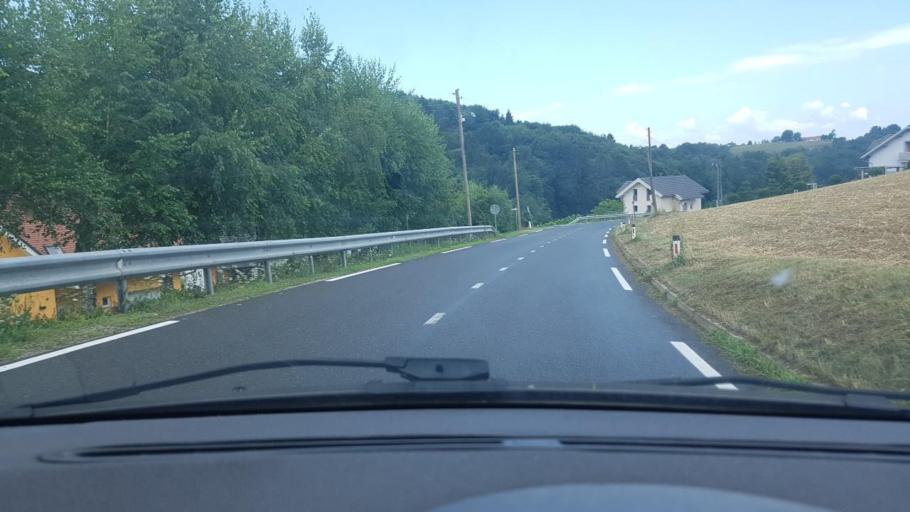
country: AT
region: Styria
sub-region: Politischer Bezirk Suedoststeiermark
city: Mureck
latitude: 46.6928
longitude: 15.7565
